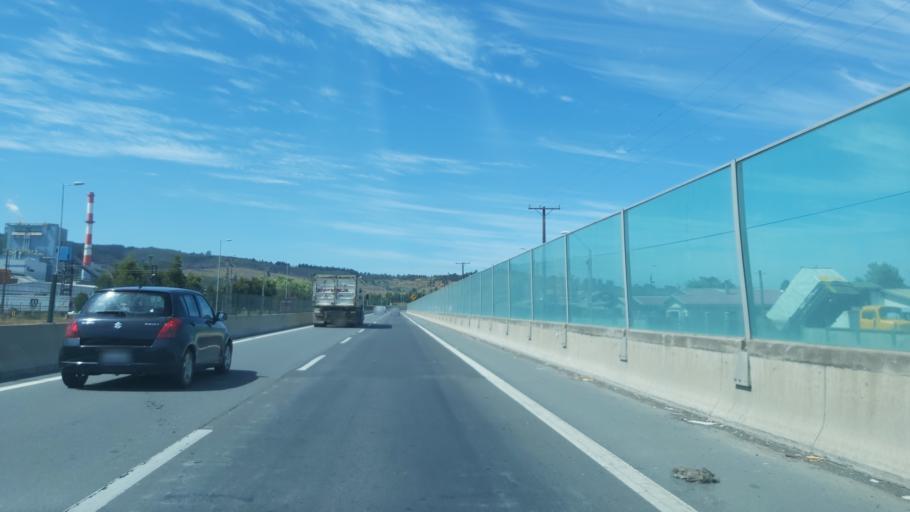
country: CL
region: Biobio
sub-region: Provincia de Concepcion
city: Coronel
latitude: -37.0354
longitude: -73.1349
